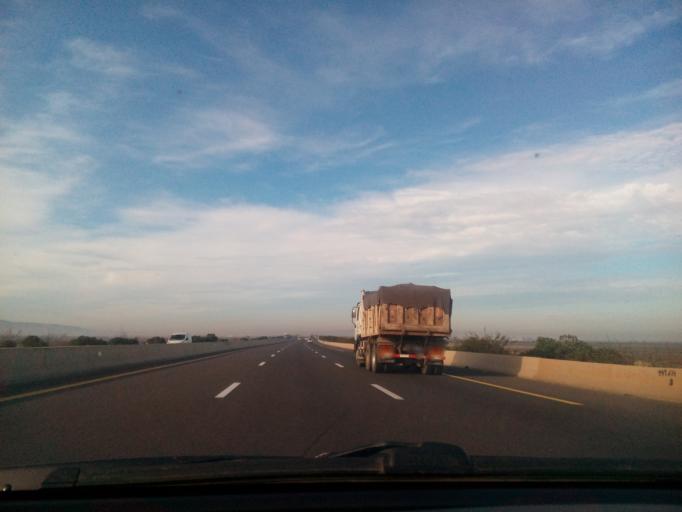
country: DZ
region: Mascara
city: Sig
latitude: 35.5877
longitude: -0.0949
